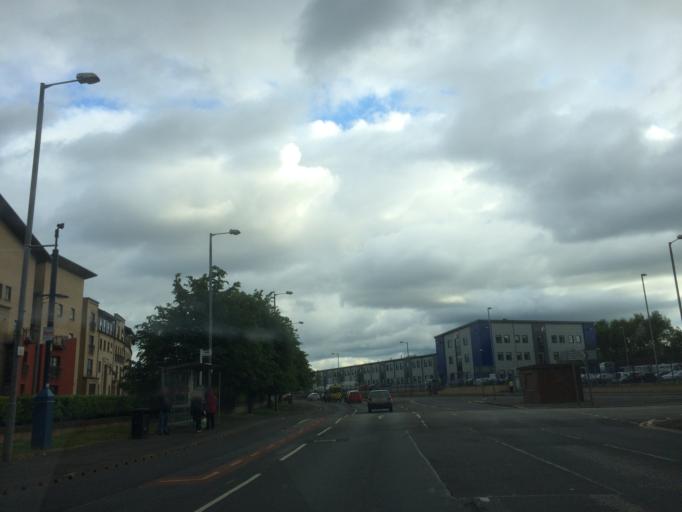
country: GB
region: Scotland
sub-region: Glasgow City
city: Glasgow
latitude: 55.8473
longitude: -4.2543
